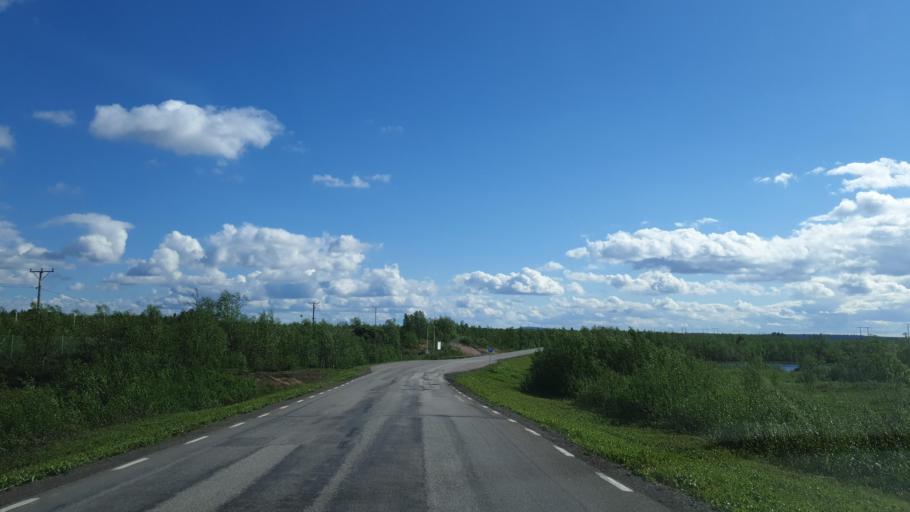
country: SE
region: Norrbotten
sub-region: Kiruna Kommun
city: Kiruna
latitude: 67.7874
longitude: 20.2291
